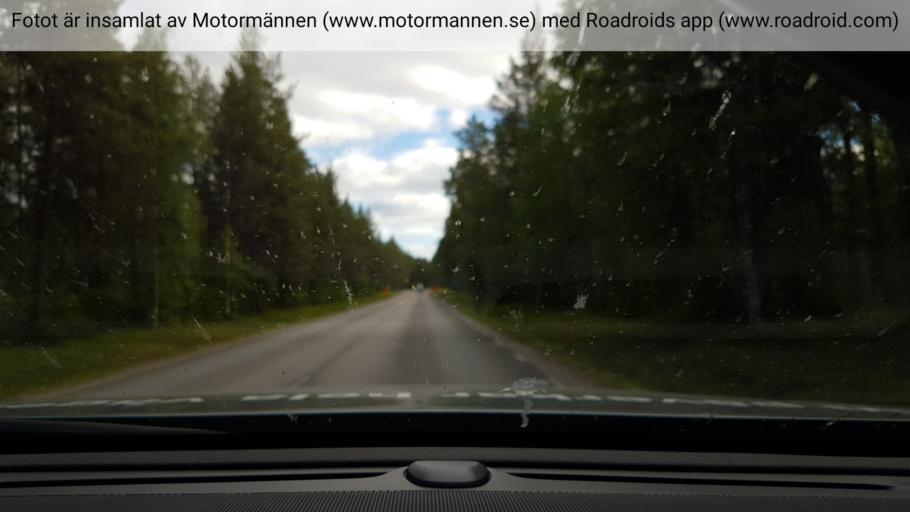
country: SE
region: Vaesterbotten
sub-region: Sorsele Kommun
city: Sorsele
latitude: 65.5466
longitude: 17.5347
